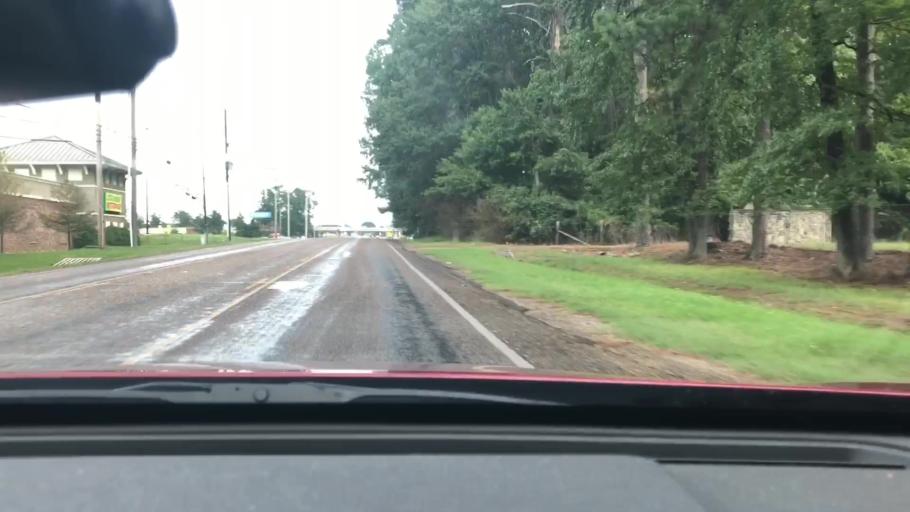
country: US
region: Texas
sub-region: Bowie County
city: Wake Village
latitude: 33.4434
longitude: -94.1031
